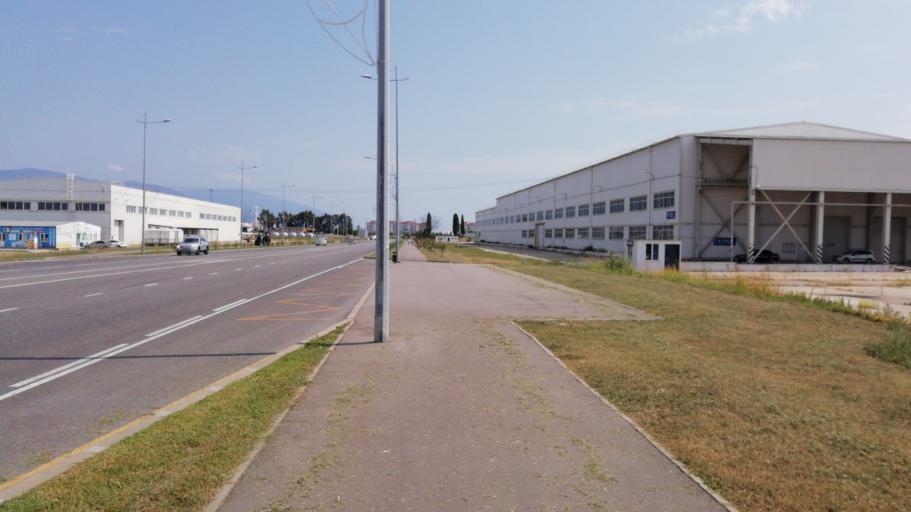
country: RU
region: Krasnodarskiy
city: Vysokoye
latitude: 43.3980
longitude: 39.9836
